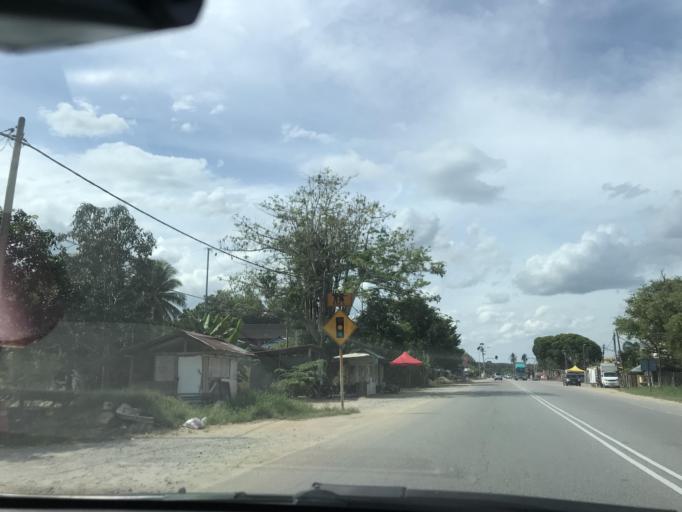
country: MY
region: Kelantan
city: Tanah Merah
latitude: 5.8523
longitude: 102.1655
